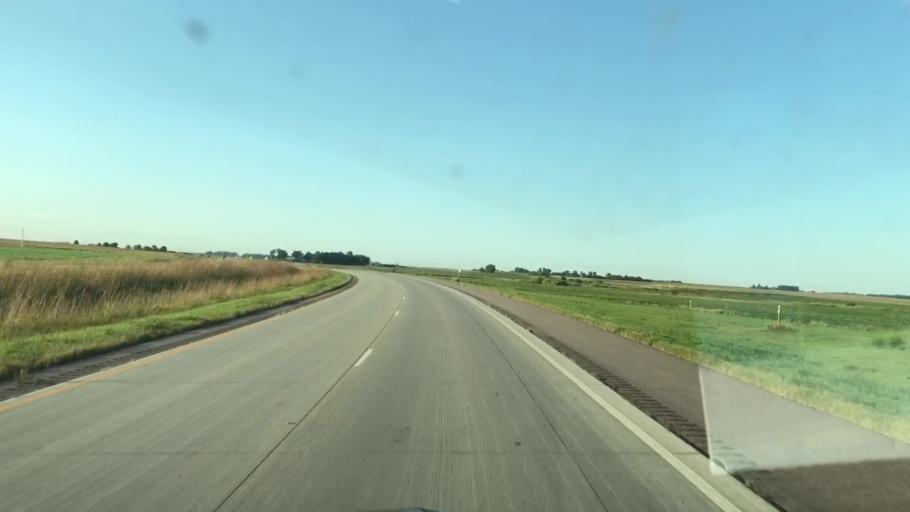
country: US
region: Minnesota
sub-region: Nobles County
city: Worthington
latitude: 43.5764
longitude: -95.6532
